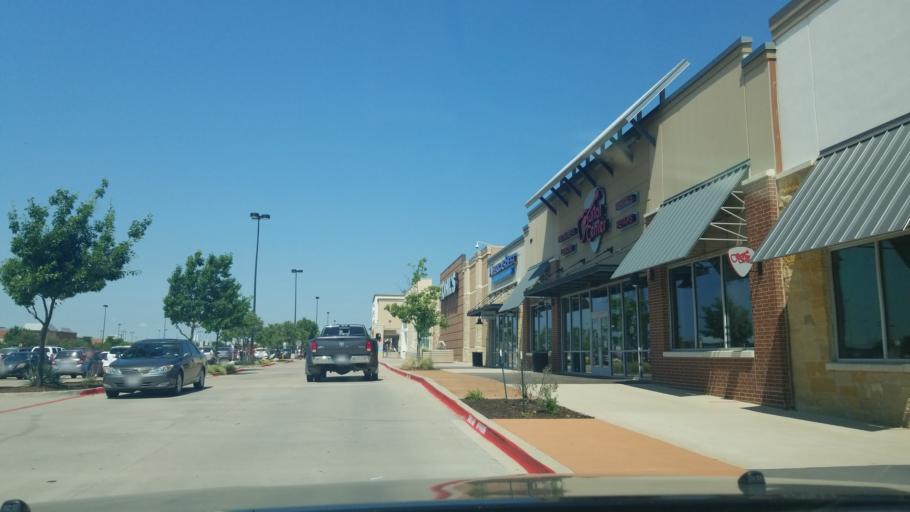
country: US
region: Texas
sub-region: Denton County
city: Denton
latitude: 33.2318
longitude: -97.1624
